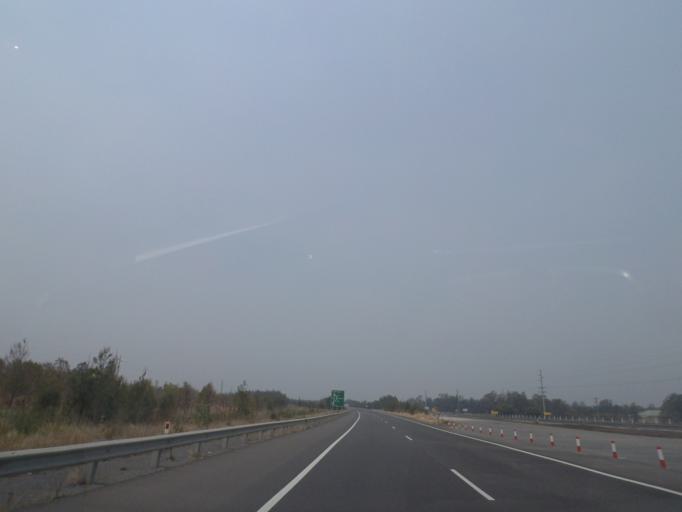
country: AU
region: New South Wales
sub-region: Ballina
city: Ballina
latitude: -28.8650
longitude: 153.5058
